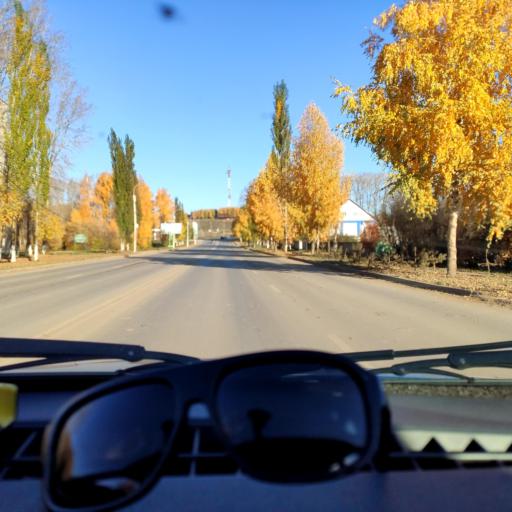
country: RU
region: Bashkortostan
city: Blagoveshchensk
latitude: 55.0533
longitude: 55.9508
